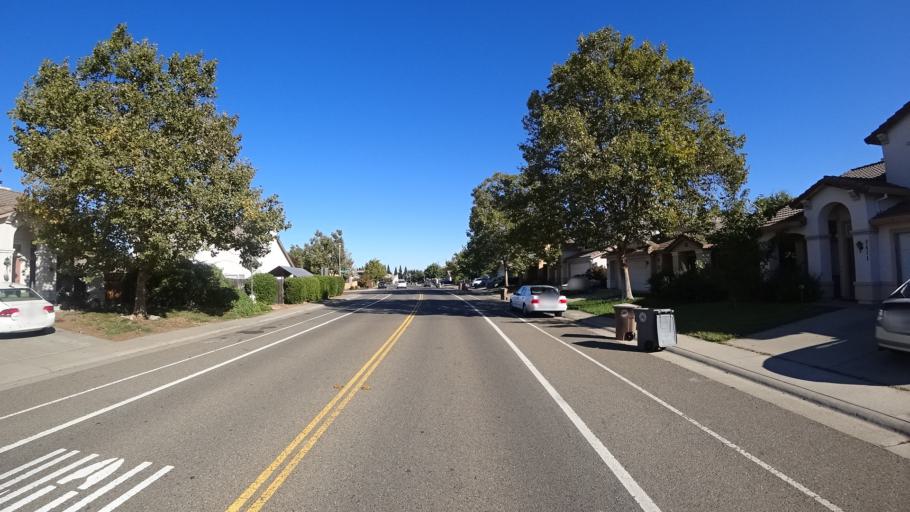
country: US
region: California
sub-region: Sacramento County
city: Vineyard
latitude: 38.4499
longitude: -121.3597
